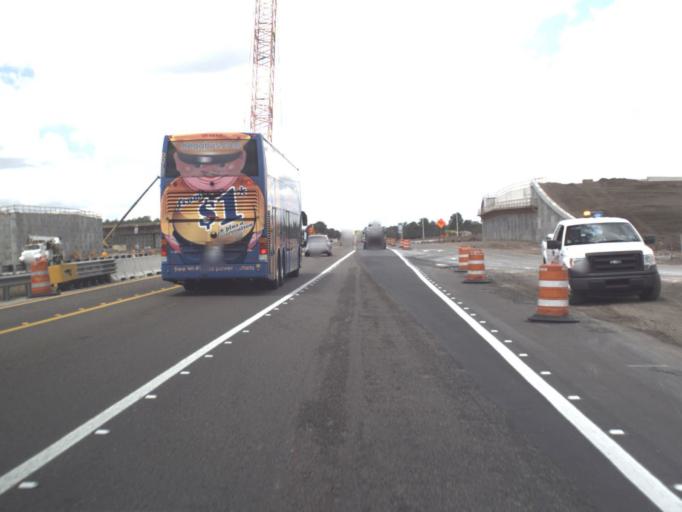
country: US
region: Florida
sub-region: Orange County
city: Wedgefield
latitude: 28.4519
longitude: -81.1690
